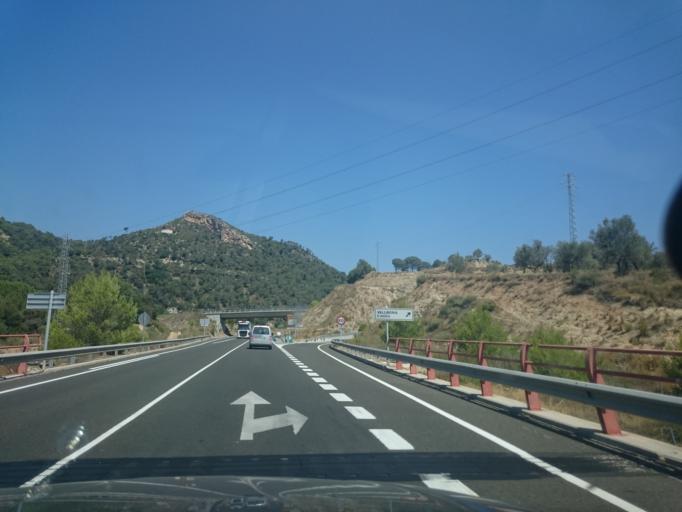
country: ES
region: Catalonia
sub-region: Provincia de Barcelona
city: Capellades
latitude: 41.5122
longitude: 1.7002
